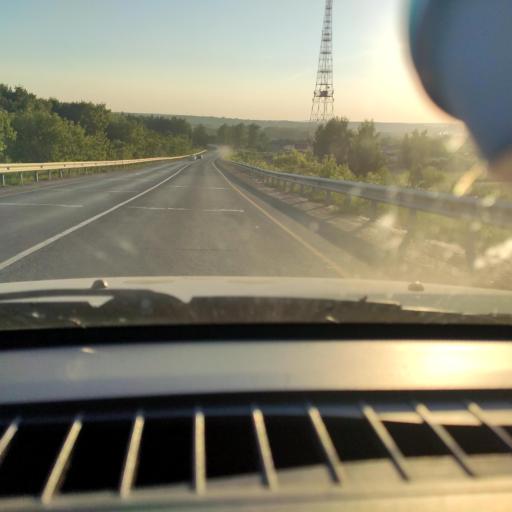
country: RU
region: Perm
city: Kungur
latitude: 57.4447
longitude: 56.9648
